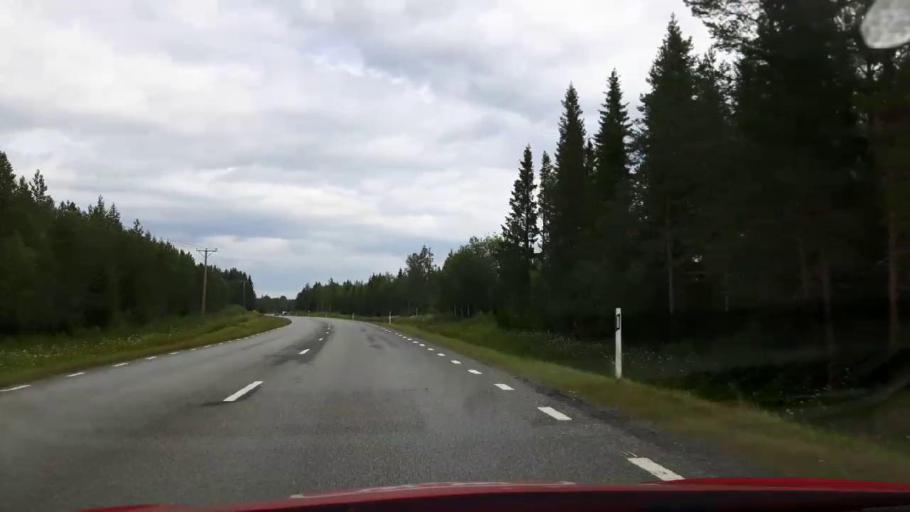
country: SE
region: Jaemtland
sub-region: Stroemsunds Kommun
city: Stroemsund
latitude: 63.6527
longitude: 15.3834
